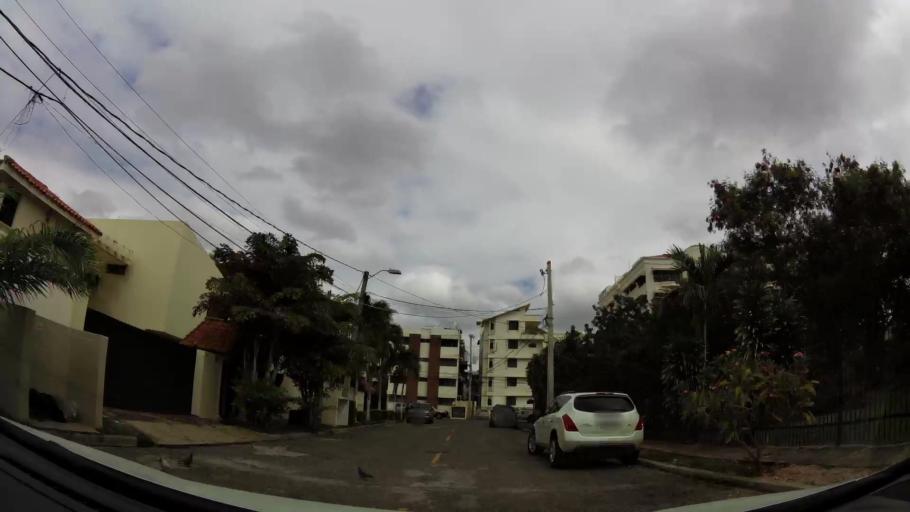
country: DO
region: Nacional
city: Bella Vista
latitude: 18.4509
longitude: -69.9447
